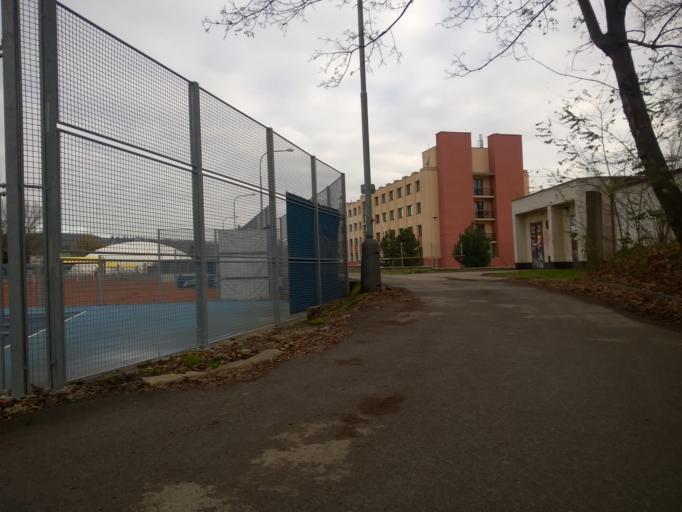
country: CZ
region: Praha
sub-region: Praha 1
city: Mala Strana
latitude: 50.1085
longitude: 14.4063
